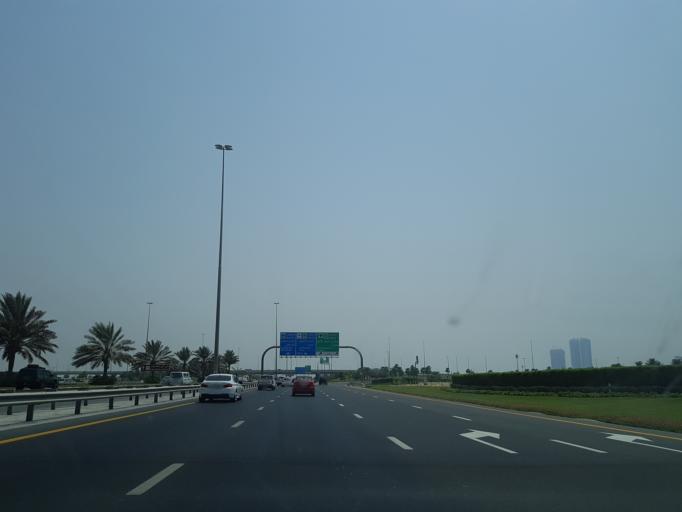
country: AE
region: Ash Shariqah
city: Sharjah
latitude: 25.2126
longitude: 55.3133
